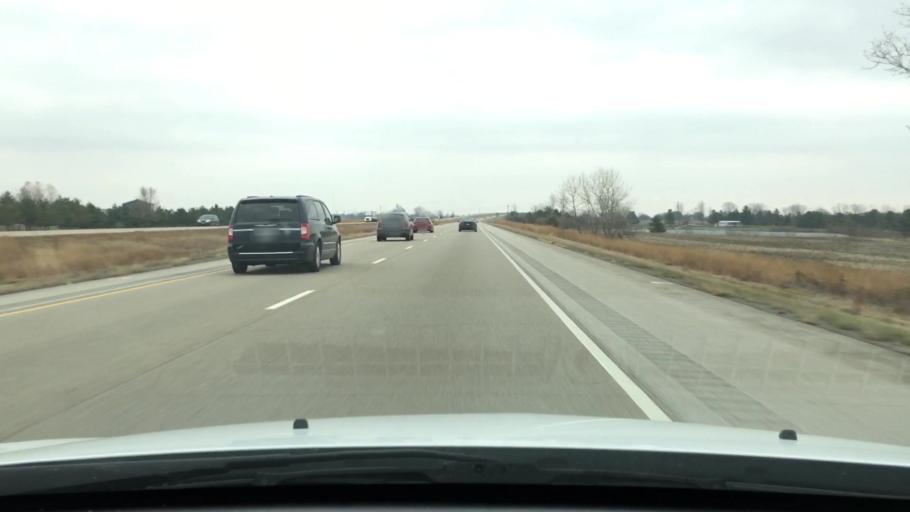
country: US
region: Illinois
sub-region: Logan County
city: Lincoln
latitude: 40.1829
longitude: -89.3376
